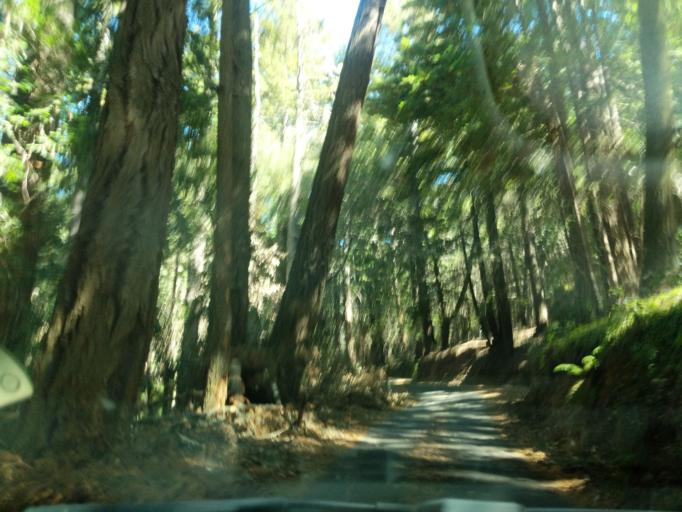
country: US
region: California
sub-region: Sonoma County
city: Monte Rio
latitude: 38.5248
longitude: -123.2375
